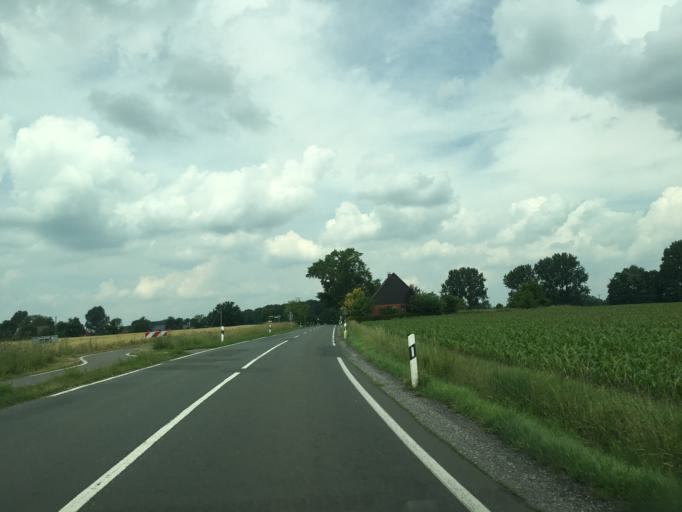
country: DE
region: North Rhine-Westphalia
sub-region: Regierungsbezirk Munster
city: Havixbeck
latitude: 51.9935
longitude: 7.3885
